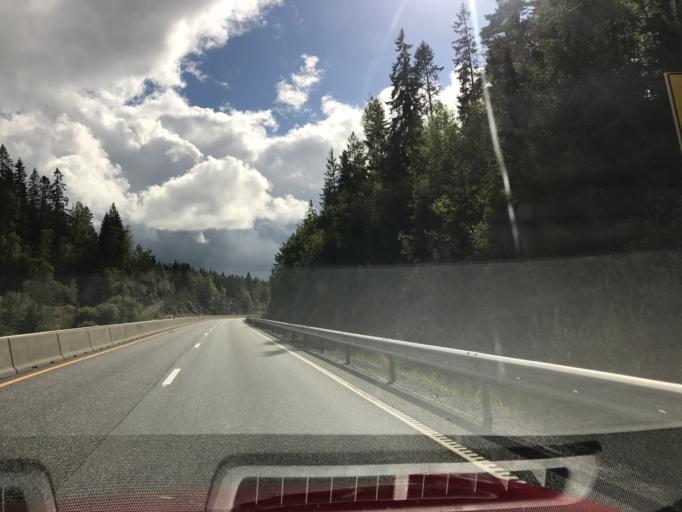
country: NO
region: Aust-Agder
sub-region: Gjerstad
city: Gjerstad
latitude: 58.8299
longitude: 9.0847
